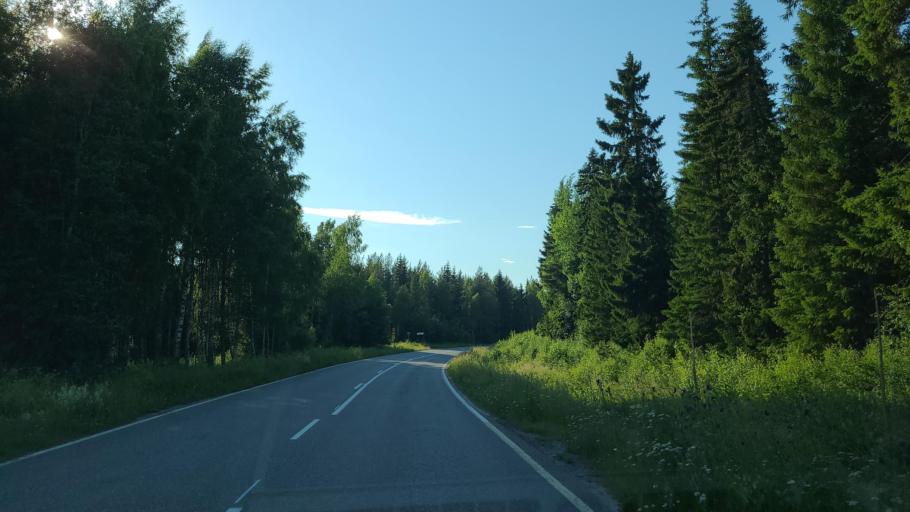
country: FI
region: Ostrobothnia
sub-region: Vaasa
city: Replot
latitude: 63.2385
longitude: 21.3889
